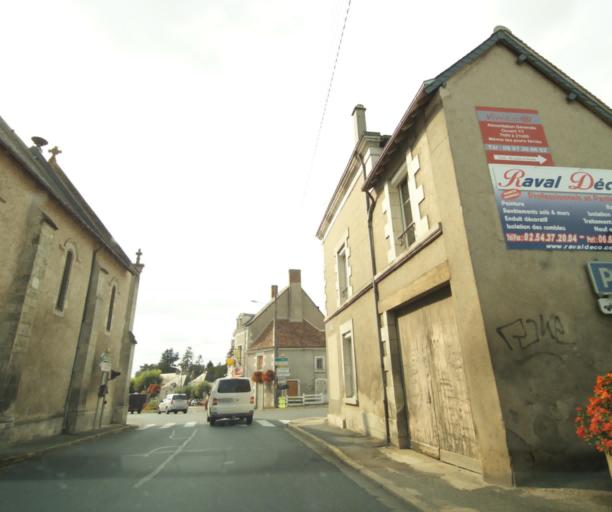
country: FR
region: Centre
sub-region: Departement de l'Indre
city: Clion
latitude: 46.9417
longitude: 1.2333
